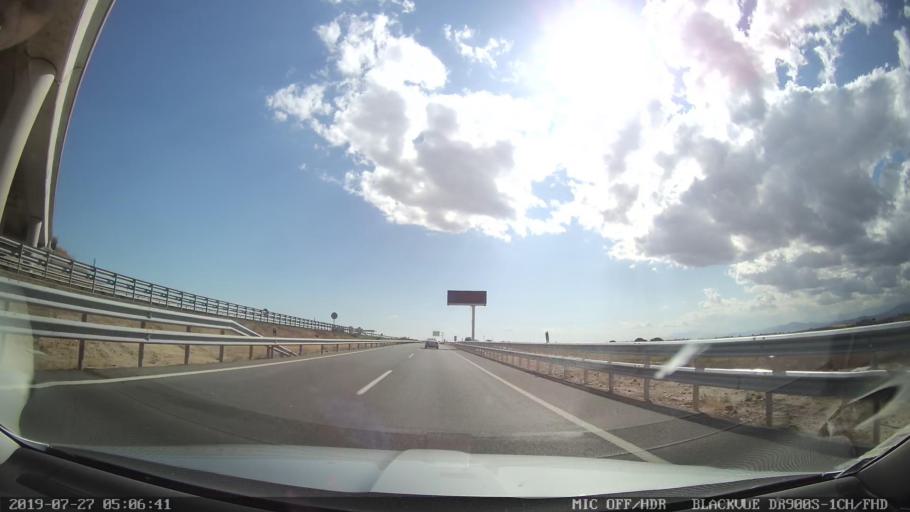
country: ES
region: Castille-La Mancha
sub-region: Province of Toledo
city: Santa Cruz del Retamar
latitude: 40.1283
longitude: -4.2160
